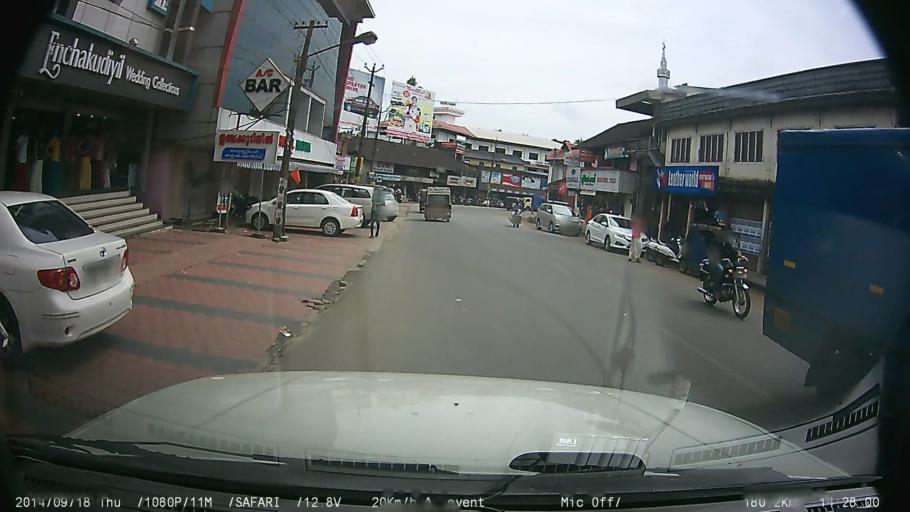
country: IN
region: Kerala
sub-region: Ernakulam
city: Kotamangalam
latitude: 10.0641
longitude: 76.6231
